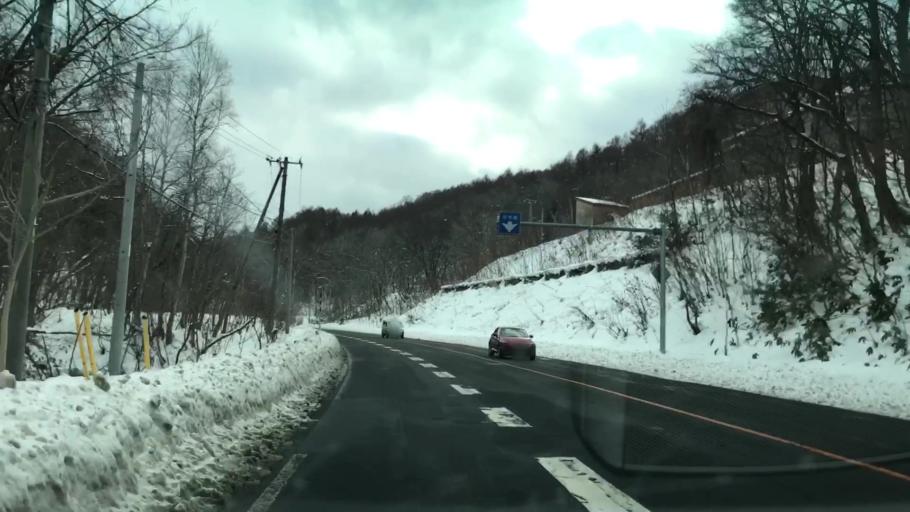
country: JP
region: Hokkaido
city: Yoichi
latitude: 43.2253
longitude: 140.7345
